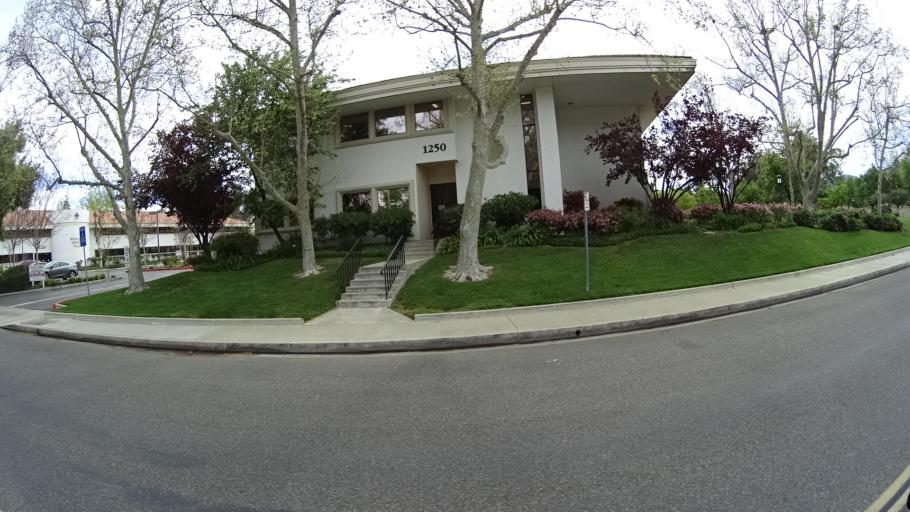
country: US
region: California
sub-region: Los Angeles County
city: Westlake Village
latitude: 34.1484
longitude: -118.8228
